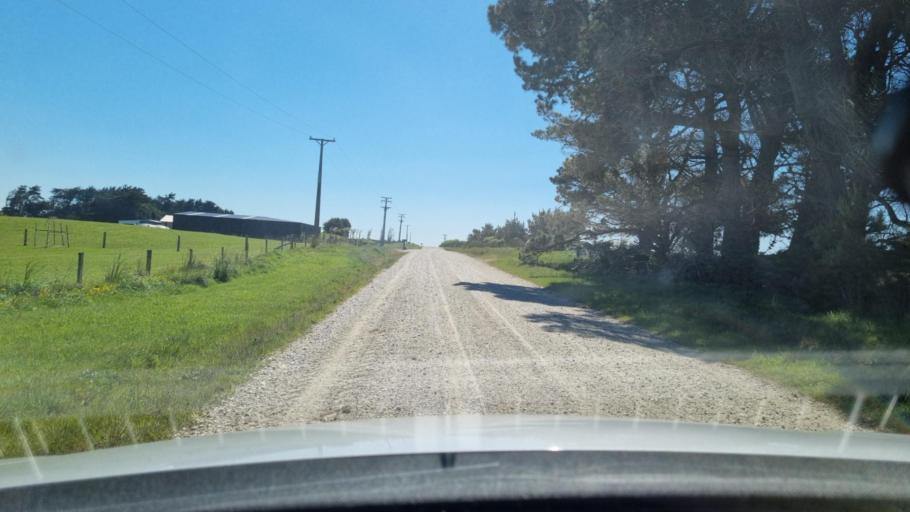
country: NZ
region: Southland
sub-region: Invercargill City
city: Invercargill
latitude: -46.4132
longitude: 168.2634
